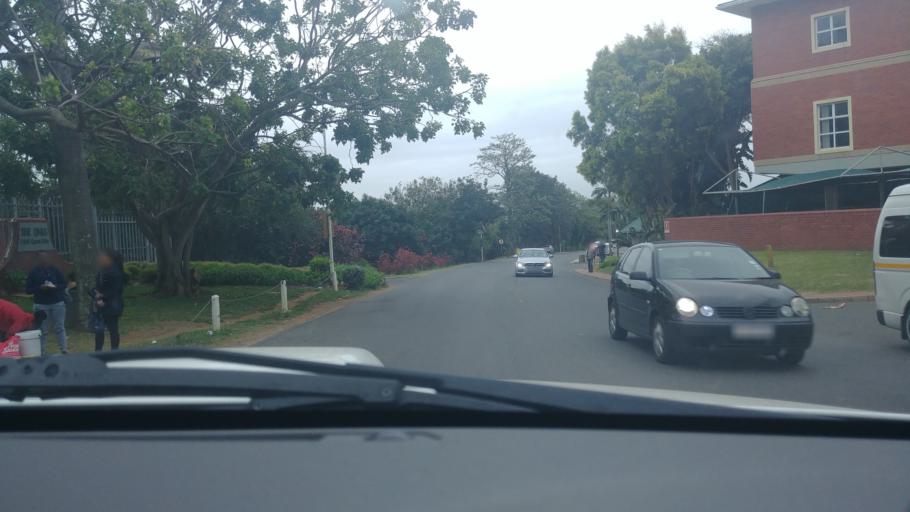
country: ZA
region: KwaZulu-Natal
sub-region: eThekwini Metropolitan Municipality
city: Durban
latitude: -29.7164
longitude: 31.0533
